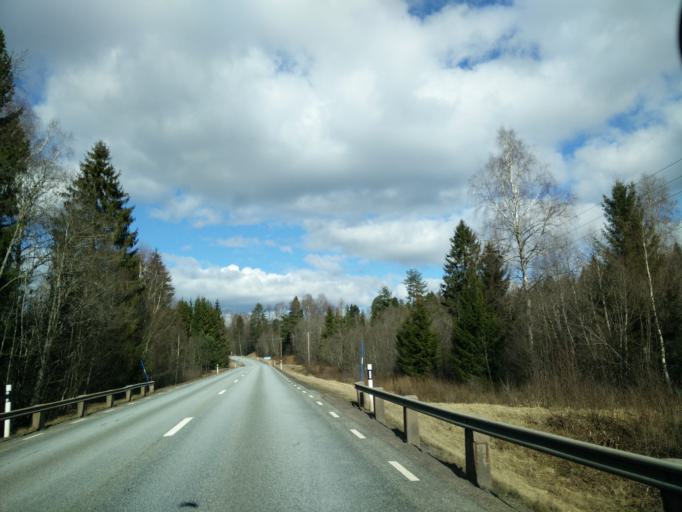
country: SE
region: Vaermland
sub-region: Munkfors Kommun
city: Munkfors
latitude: 59.9117
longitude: 13.5691
